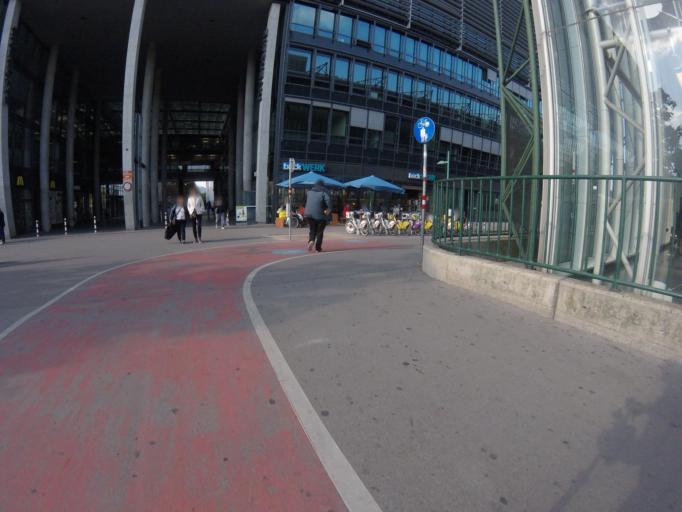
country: NE
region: Dosso
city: Dosso
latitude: 12.6804
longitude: 3.0455
